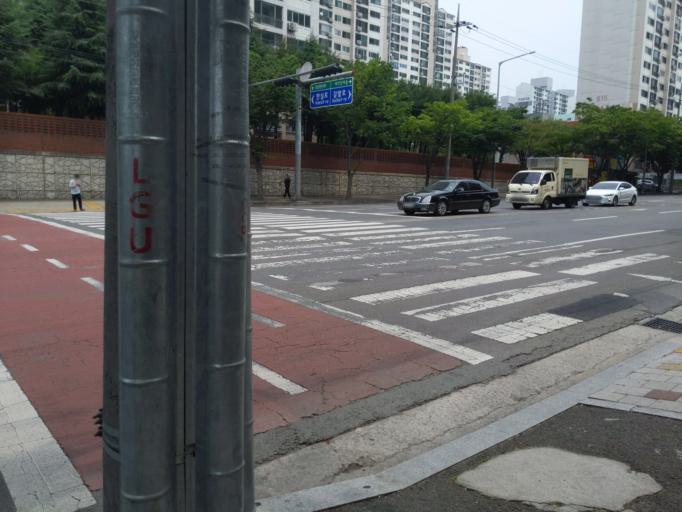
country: KR
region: Daegu
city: Hwawon
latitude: 35.8074
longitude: 128.5285
